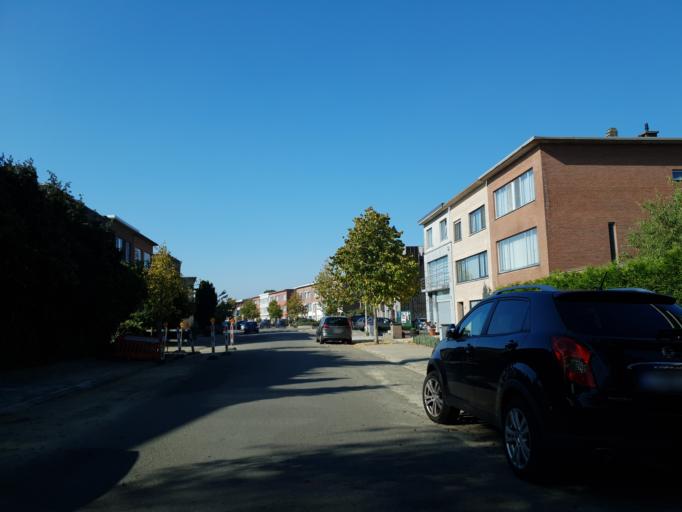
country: BE
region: Flanders
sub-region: Provincie Antwerpen
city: Borsbeek
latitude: 51.2004
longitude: 4.4792
